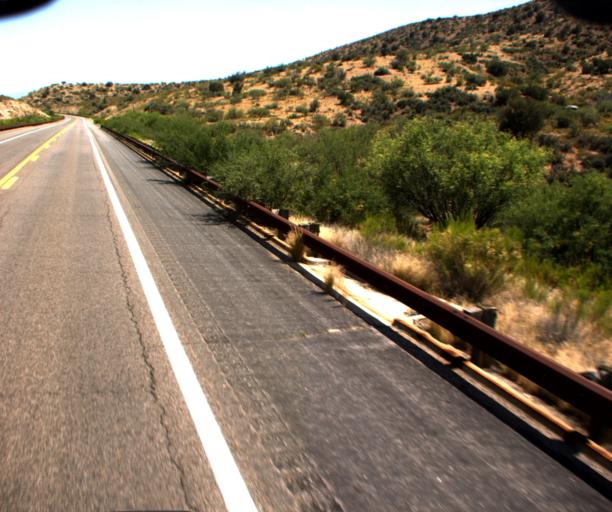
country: US
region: Arizona
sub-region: Gila County
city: Claypool
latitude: 33.4997
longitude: -110.8668
